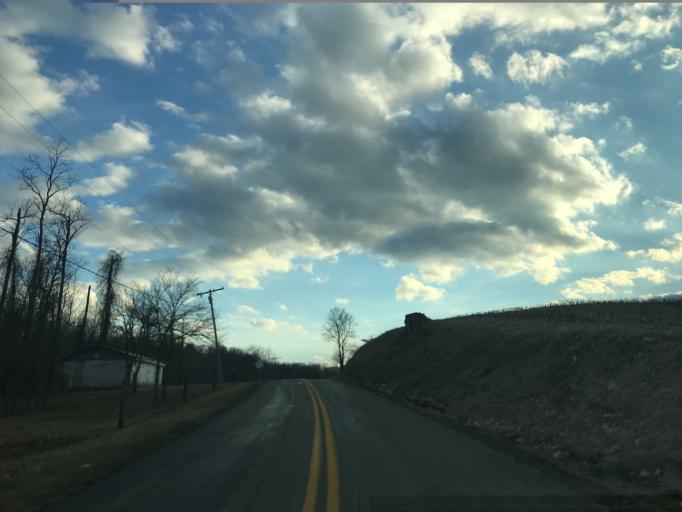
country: US
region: Maryland
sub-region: Harford County
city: Jarrettsville
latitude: 39.6062
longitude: -76.4311
